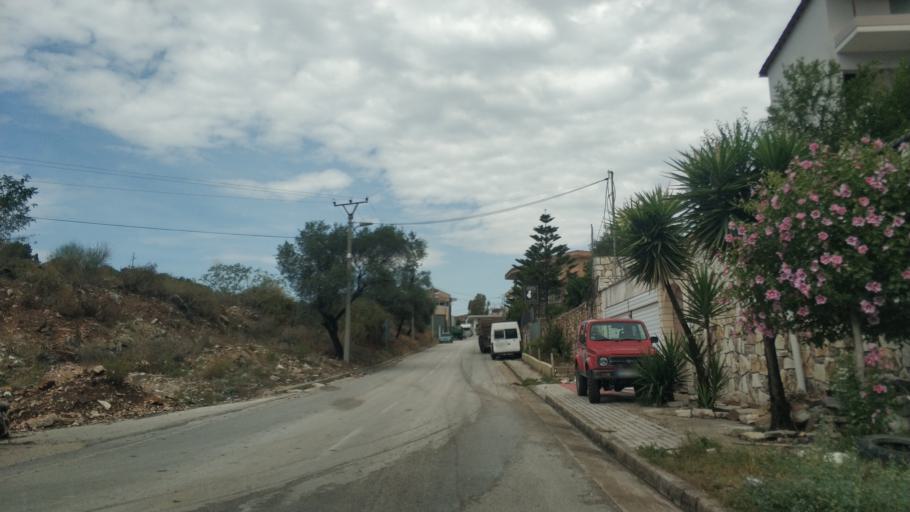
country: AL
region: Vlore
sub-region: Rrethi i Sarandes
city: Sarande
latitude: 39.8737
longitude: 20.0298
